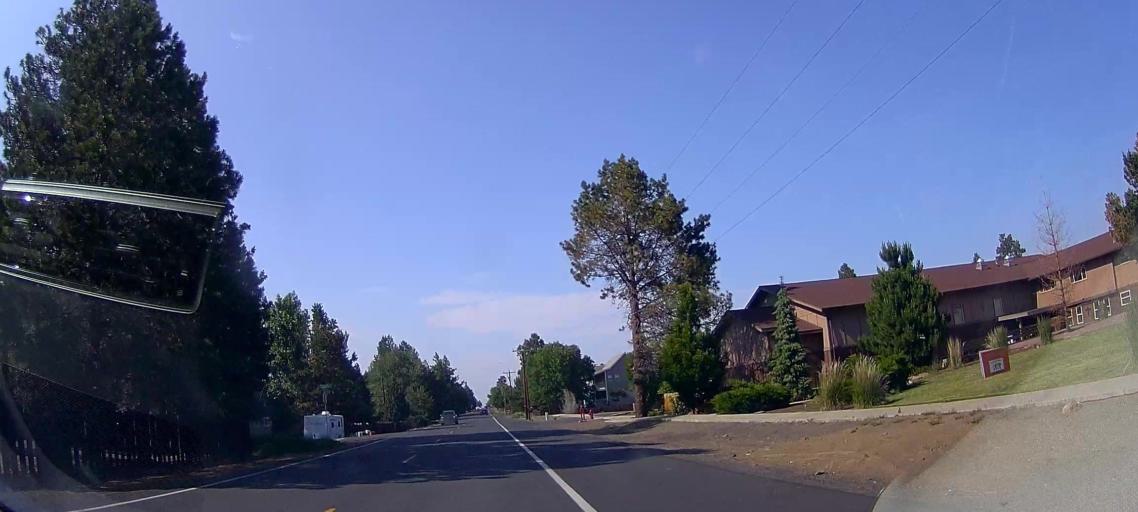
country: US
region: Oregon
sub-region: Deschutes County
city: Bend
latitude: 44.0399
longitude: -121.2687
